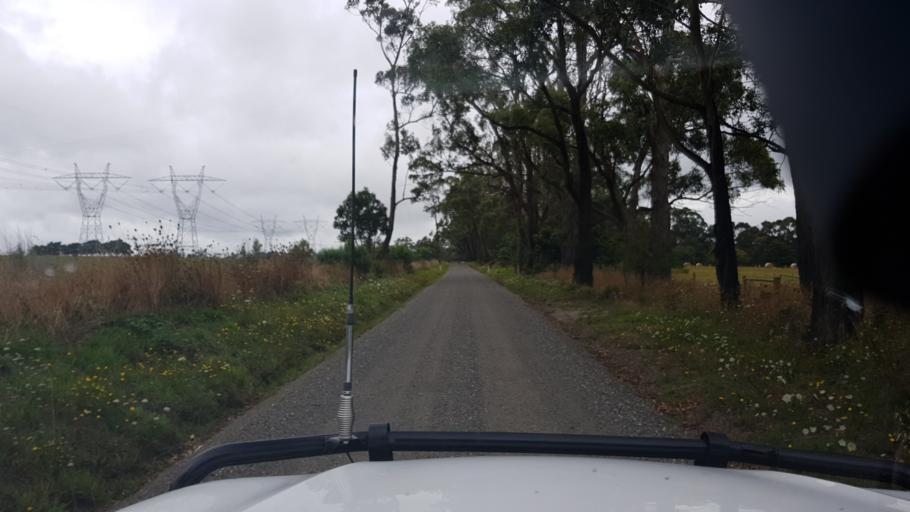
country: AU
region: Victoria
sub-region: Baw Baw
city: Warragul
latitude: -38.1896
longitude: 145.8460
